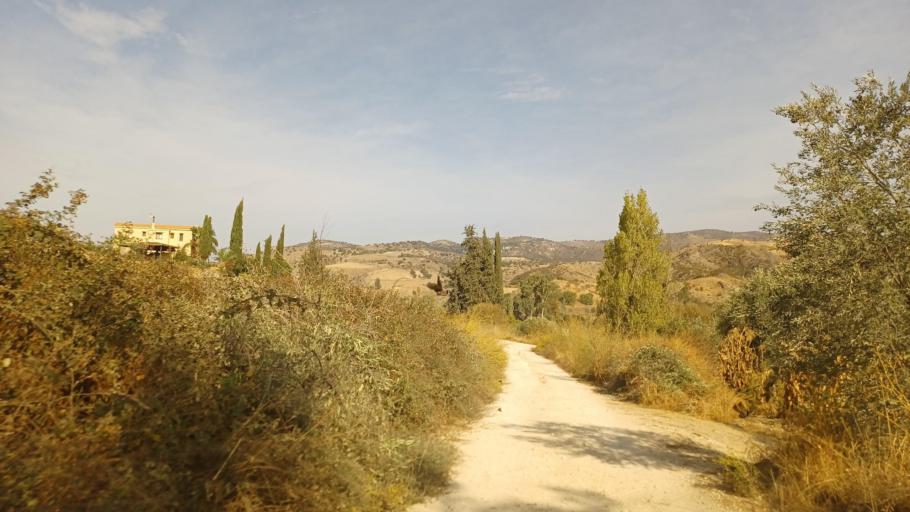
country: CY
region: Pafos
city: Polis
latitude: 34.9524
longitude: 32.5142
